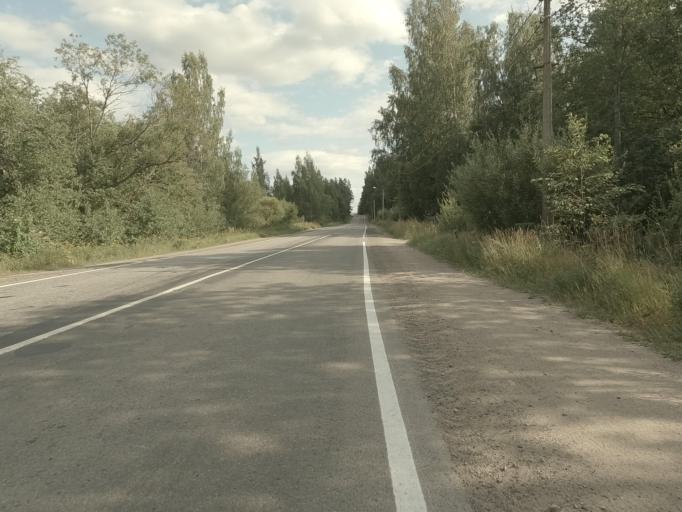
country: RU
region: Leningrad
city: Kamennogorsk
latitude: 60.9396
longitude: 29.1555
